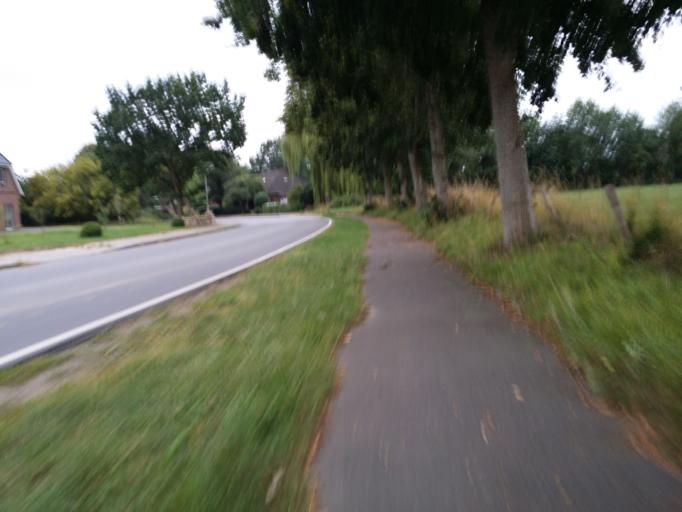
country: DE
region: Schleswig-Holstein
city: Huje
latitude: 53.9803
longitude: 9.4322
